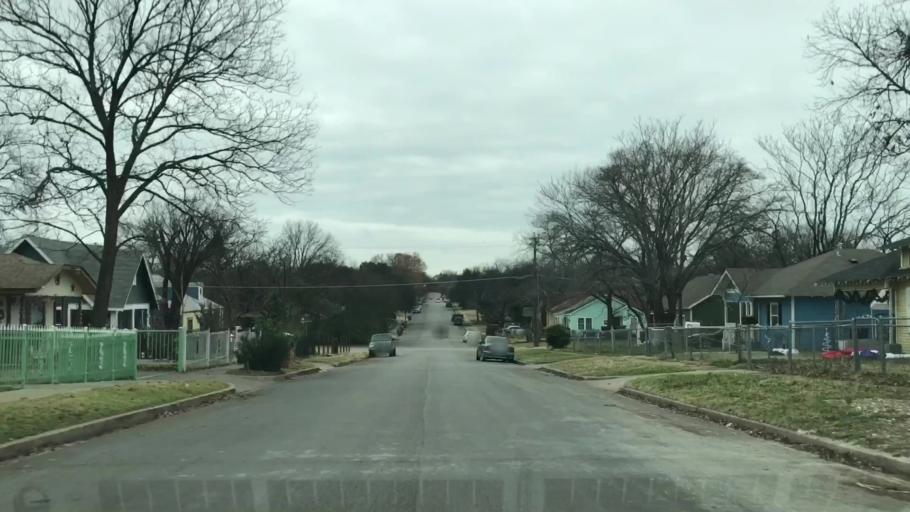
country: US
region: Texas
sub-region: Dallas County
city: Cockrell Hill
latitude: 32.7380
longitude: -96.8492
